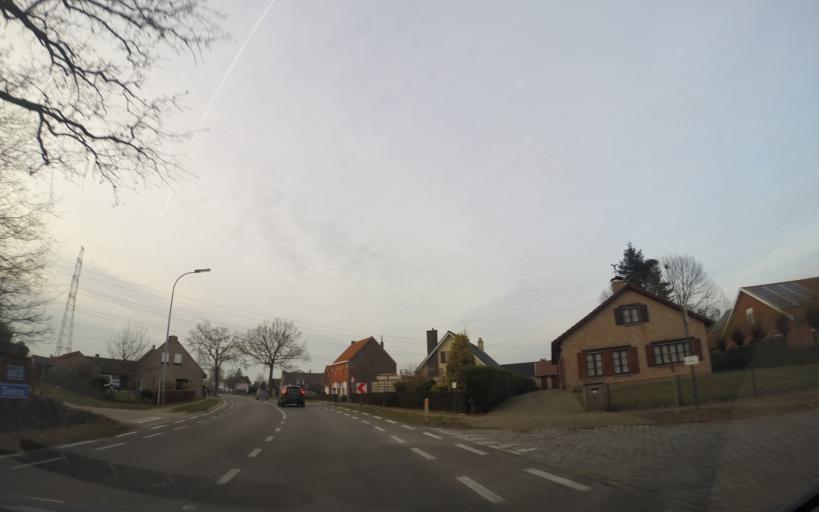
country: BE
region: Flanders
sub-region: Provincie Oost-Vlaanderen
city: Deinze
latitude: 50.9963
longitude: 3.5010
